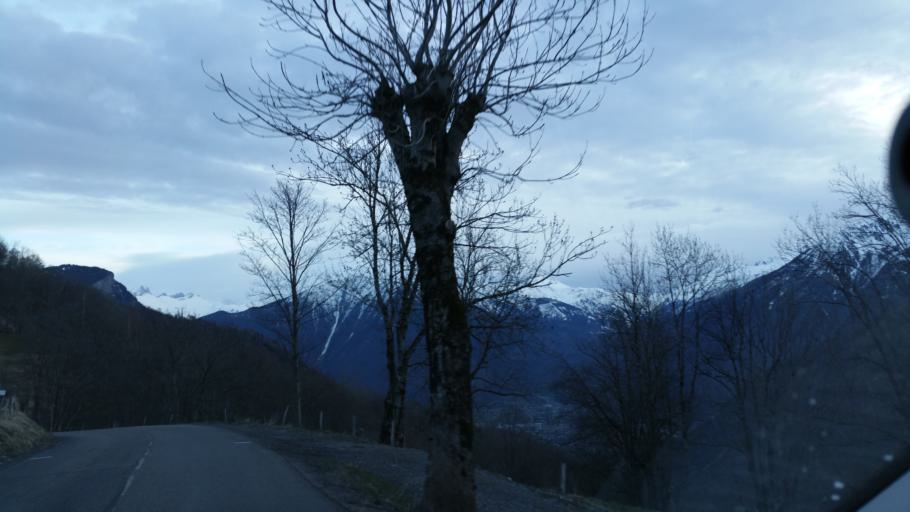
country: FR
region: Rhone-Alpes
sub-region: Departement de la Savoie
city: La Chambre
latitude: 45.3971
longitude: 6.3359
